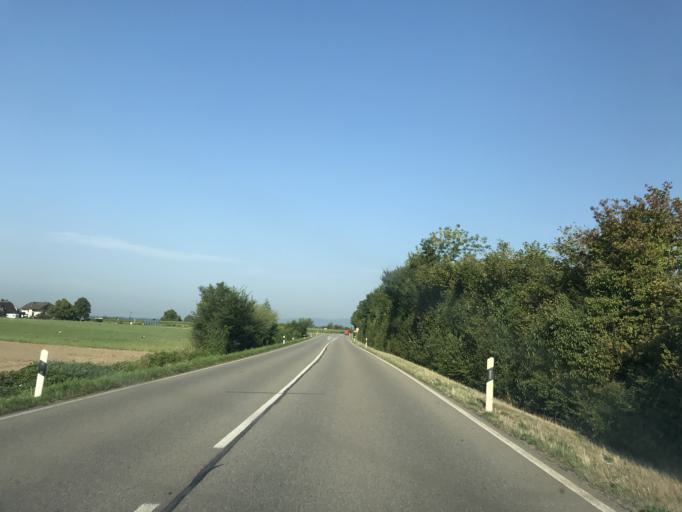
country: DE
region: Baden-Wuerttemberg
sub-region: Freiburg Region
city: Heuweiler
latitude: 48.0573
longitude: 7.9105
